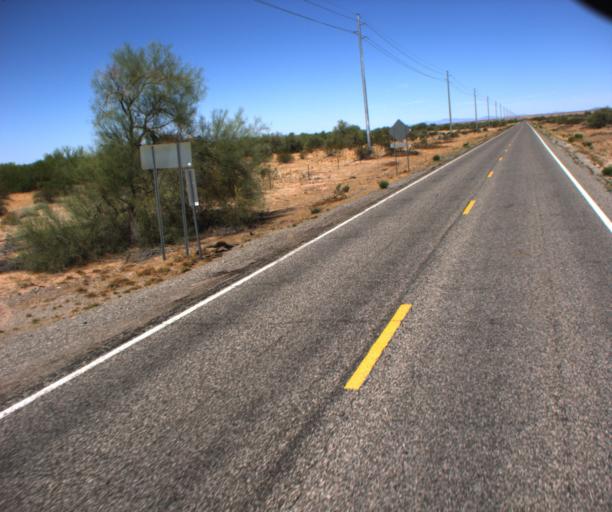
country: US
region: Arizona
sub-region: La Paz County
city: Cienega Springs
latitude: 33.9766
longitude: -114.0508
